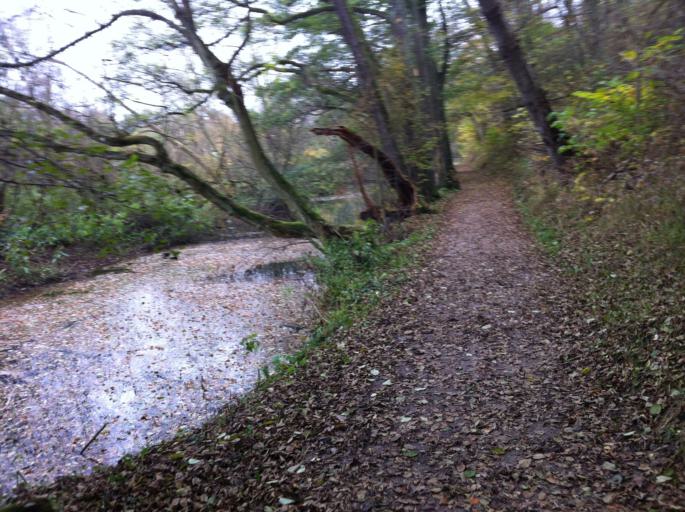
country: SE
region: Skane
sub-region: Helsingborg
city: Gantofta
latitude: 55.9974
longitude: 12.7925
